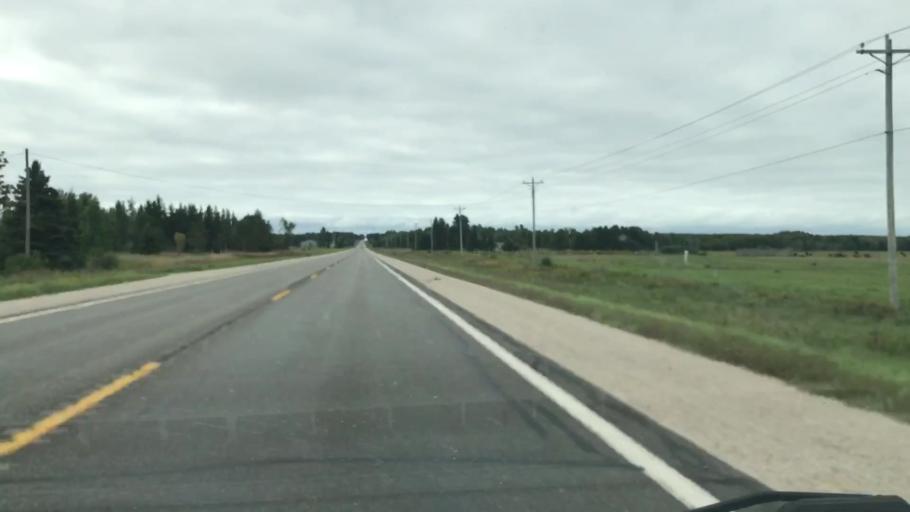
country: US
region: Michigan
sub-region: Luce County
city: Newberry
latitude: 46.1451
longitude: -85.5713
